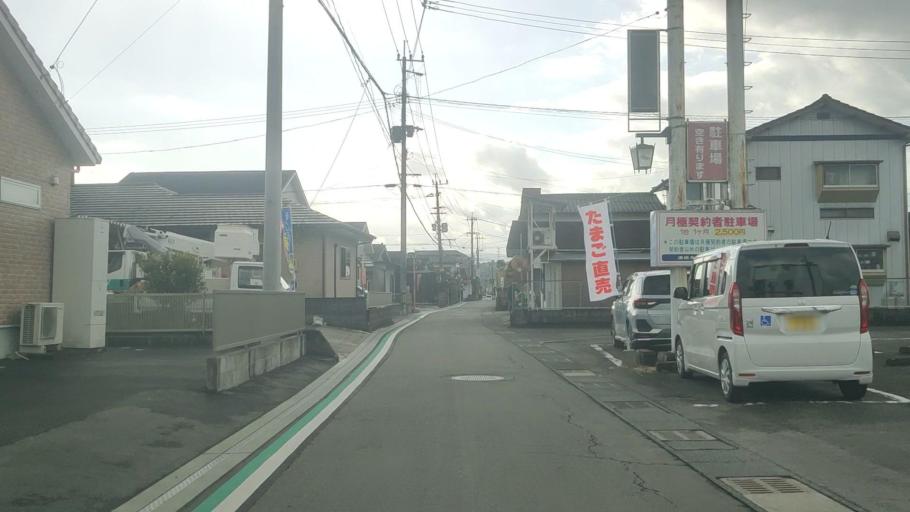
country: JP
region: Kumamoto
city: Hitoyoshi
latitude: 32.2216
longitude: 130.7714
